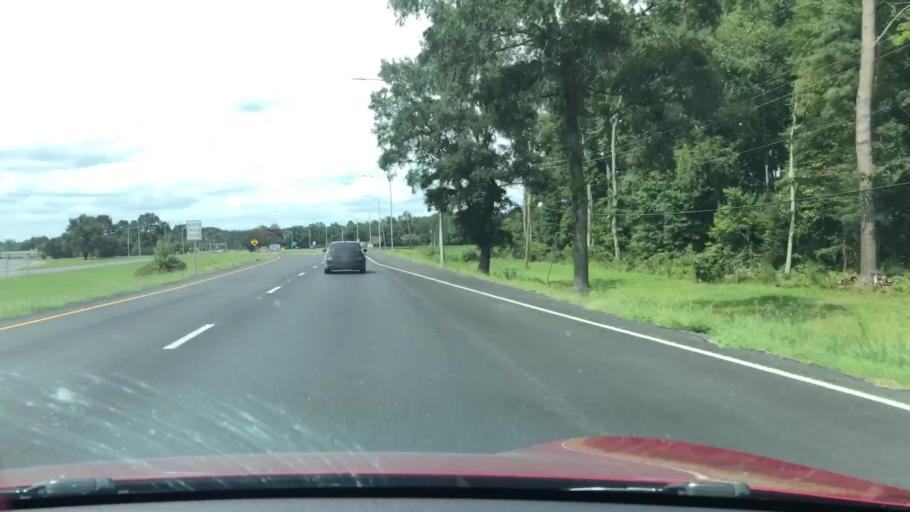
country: US
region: Maryland
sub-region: Worcester County
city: Pocomoke City
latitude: 38.0557
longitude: -75.5438
